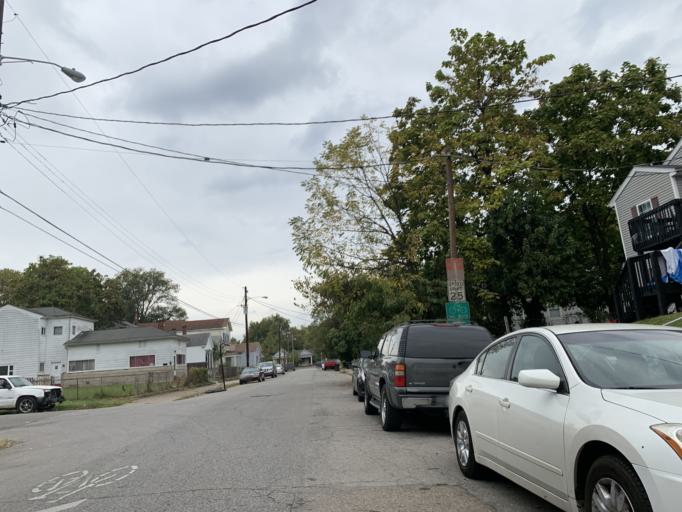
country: US
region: Kentucky
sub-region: Jefferson County
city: Louisville
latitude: 38.2419
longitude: -85.7829
